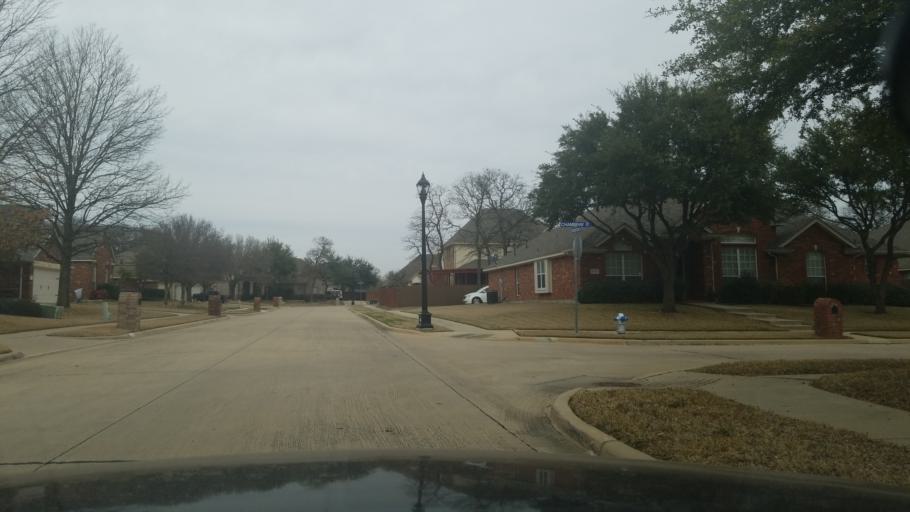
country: US
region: Texas
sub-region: Denton County
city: Corinth
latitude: 33.1334
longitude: -97.0760
